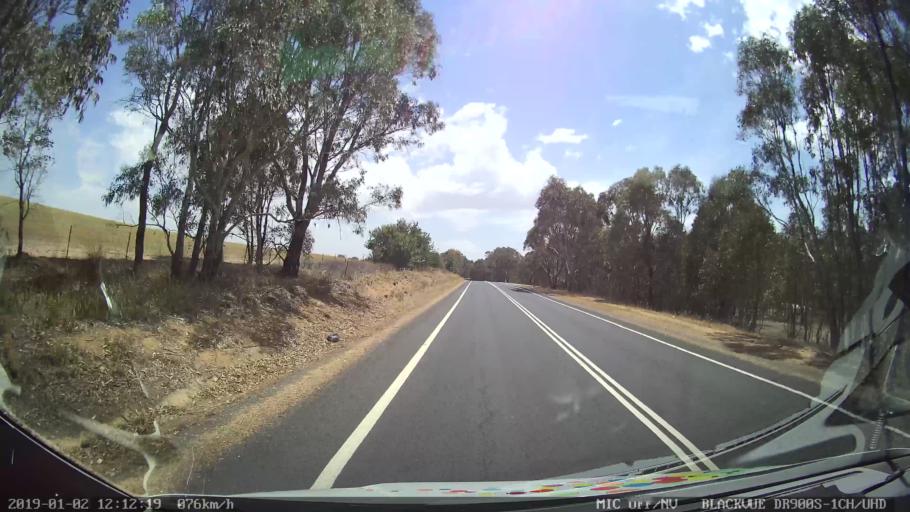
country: AU
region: New South Wales
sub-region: Young
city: Young
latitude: -34.4383
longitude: 148.2549
